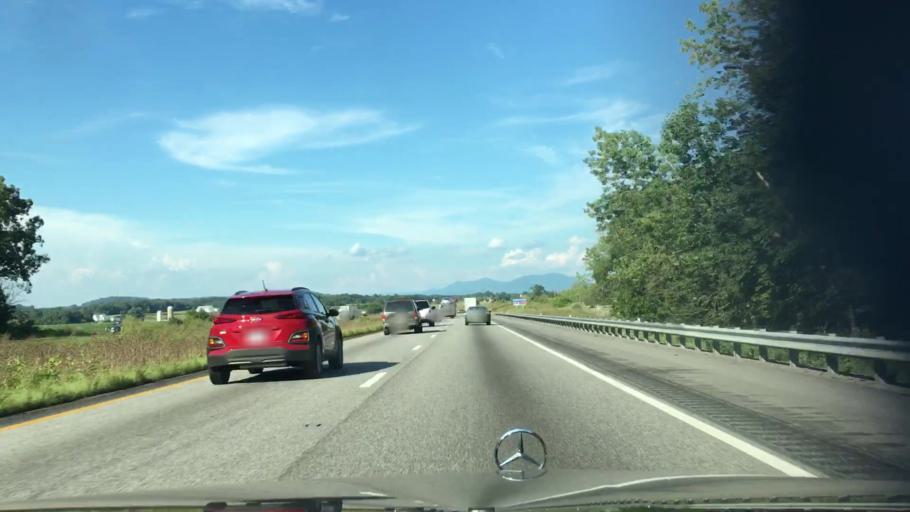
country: US
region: Virginia
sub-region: Augusta County
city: Weyers Cave
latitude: 38.2592
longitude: -78.9474
